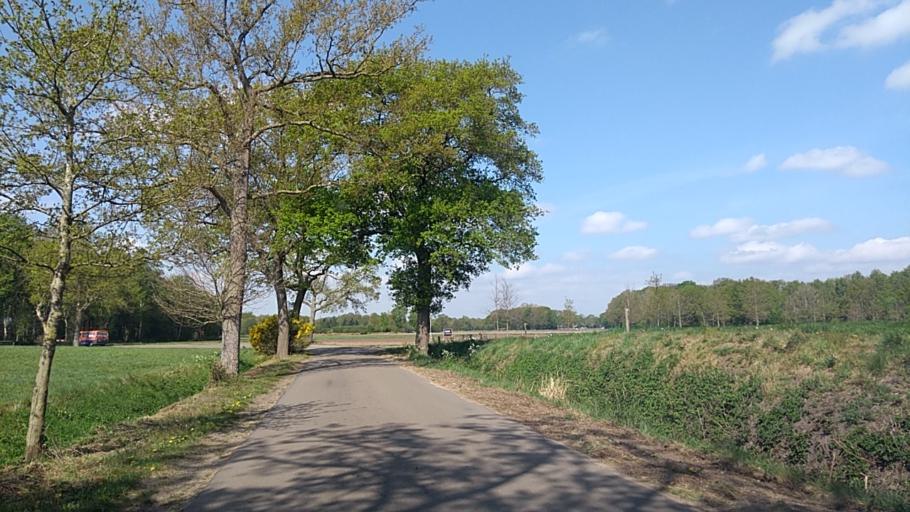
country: NL
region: Overijssel
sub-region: Gemeente Haaksbergen
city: Haaksbergen
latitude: 52.1392
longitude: 6.7084
